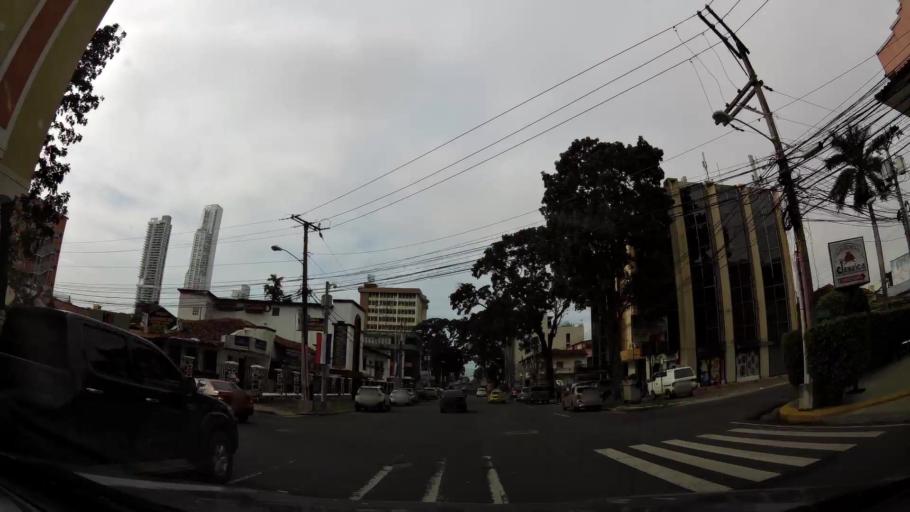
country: PA
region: Panama
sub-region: Distrito de Panama
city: Ancon
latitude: 8.9727
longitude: -79.5341
